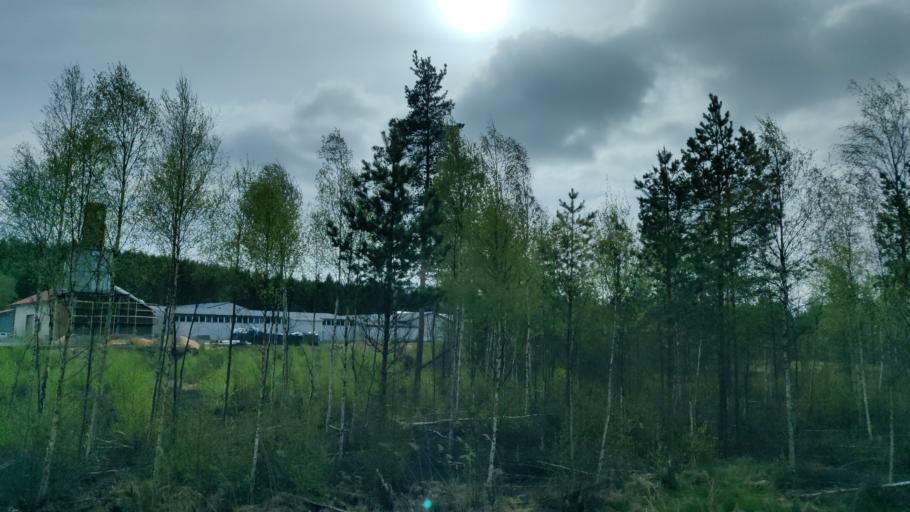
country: SE
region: Vaermland
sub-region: Forshaga Kommun
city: Deje
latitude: 59.6201
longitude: 13.4471
